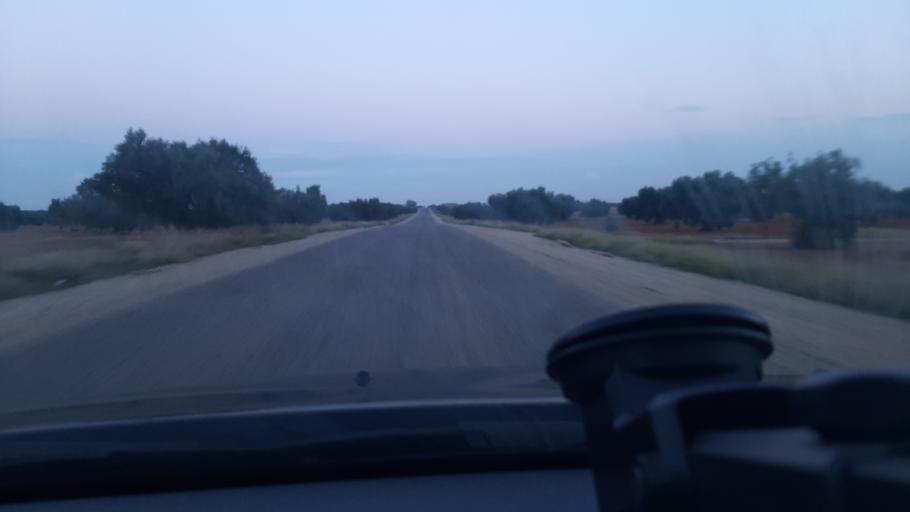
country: TN
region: Al Mahdiyah
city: Shurban
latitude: 35.0297
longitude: 10.4836
